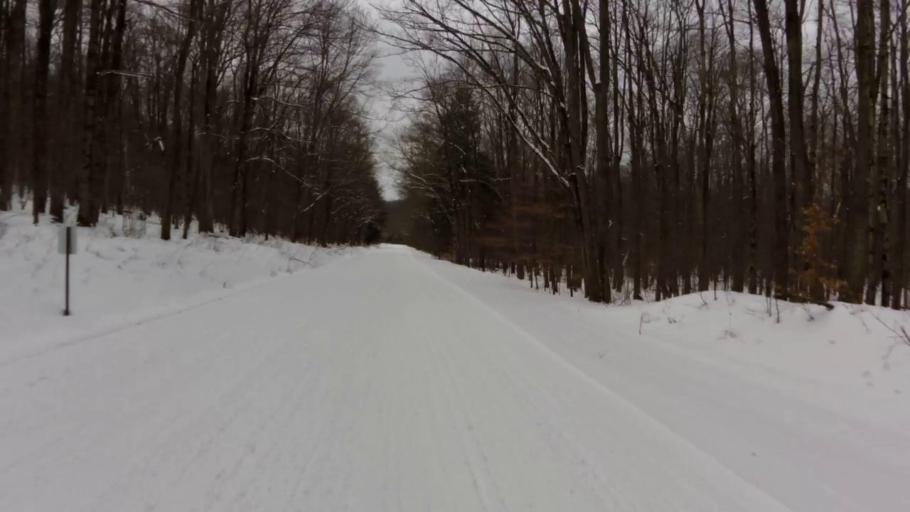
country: US
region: New York
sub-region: Cattaraugus County
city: Salamanca
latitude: 42.0346
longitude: -78.7949
